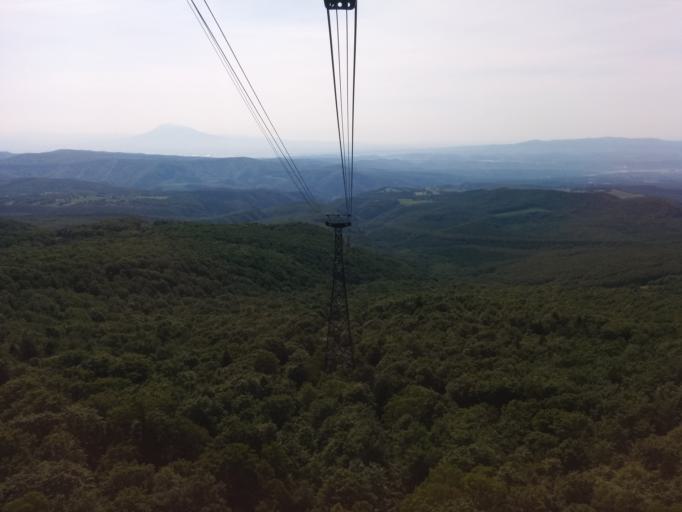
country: JP
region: Aomori
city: Aomori Shi
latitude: 40.6779
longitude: 140.8482
